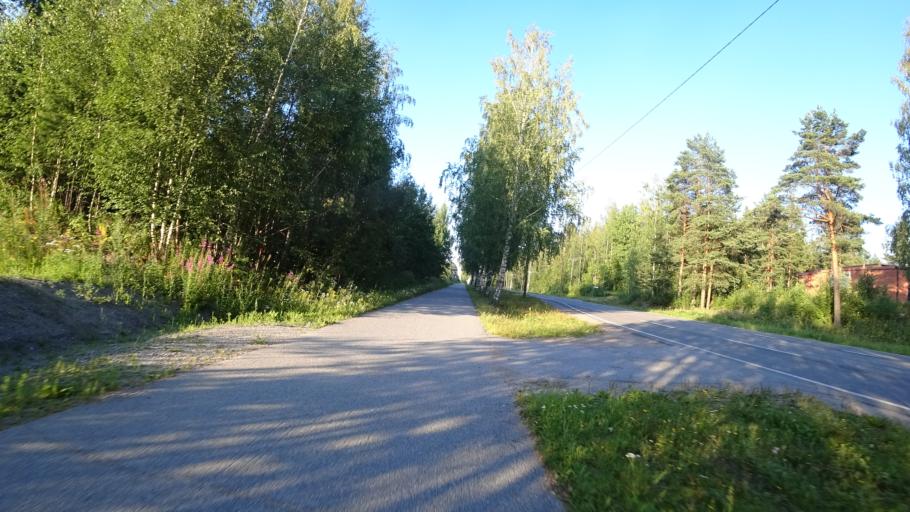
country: FI
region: Pirkanmaa
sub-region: Tampere
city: Nokia
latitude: 61.4690
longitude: 23.4520
